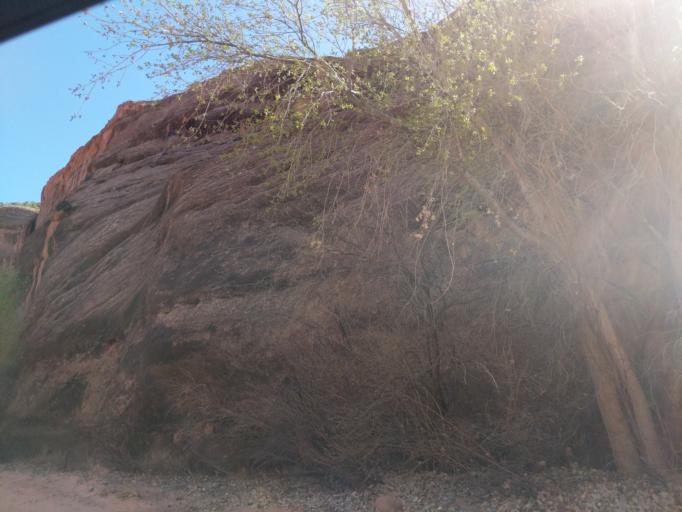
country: US
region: Arizona
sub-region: Apache County
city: Chinle
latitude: 36.1588
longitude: -109.4606
